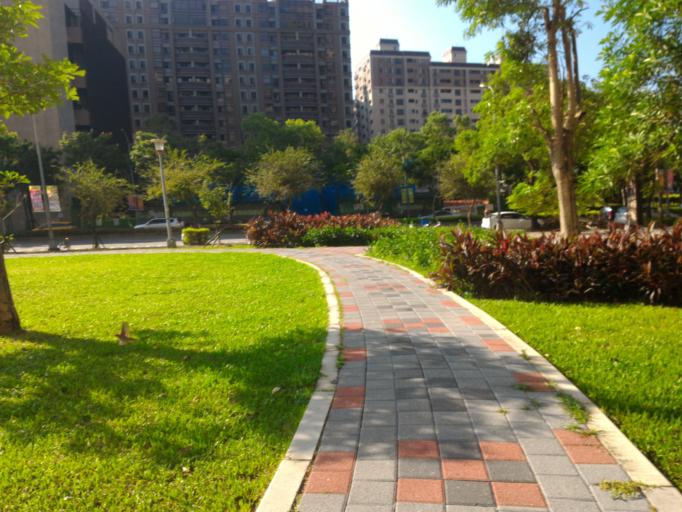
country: TW
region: Taiwan
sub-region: Taoyuan
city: Taoyuan
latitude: 24.9447
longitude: 121.3774
